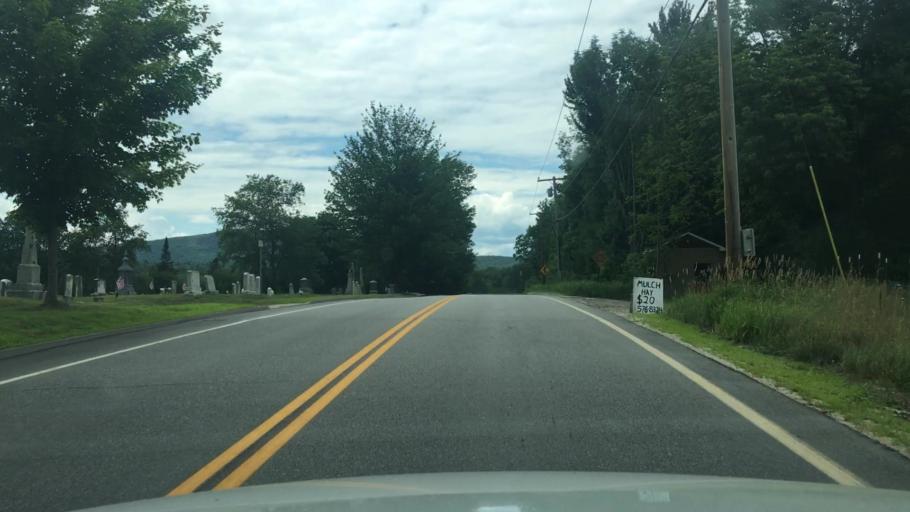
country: US
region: Maine
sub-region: Oxford County
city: Paris
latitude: 44.3685
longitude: -70.4636
